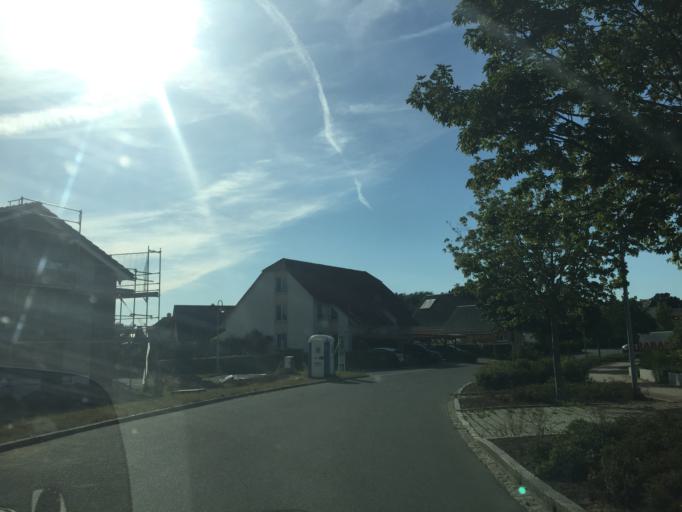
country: DE
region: Thuringia
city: Schmolln
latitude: 50.8860
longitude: 12.3614
